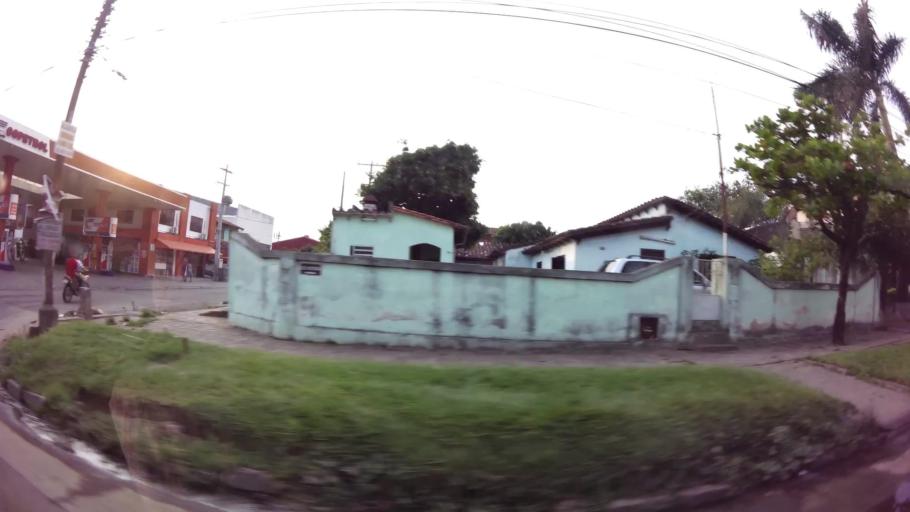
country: PY
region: Central
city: Lambare
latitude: -25.3332
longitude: -57.5891
